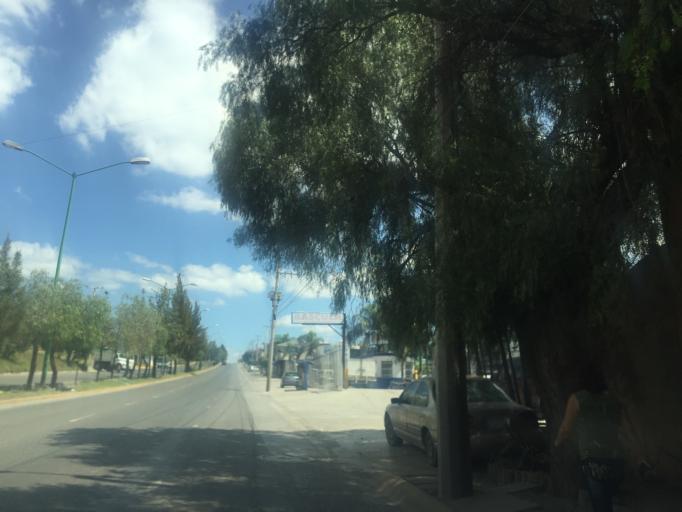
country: MX
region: Guanajuato
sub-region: Leon
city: Ejido la Joya
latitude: 21.1228
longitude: -101.7207
